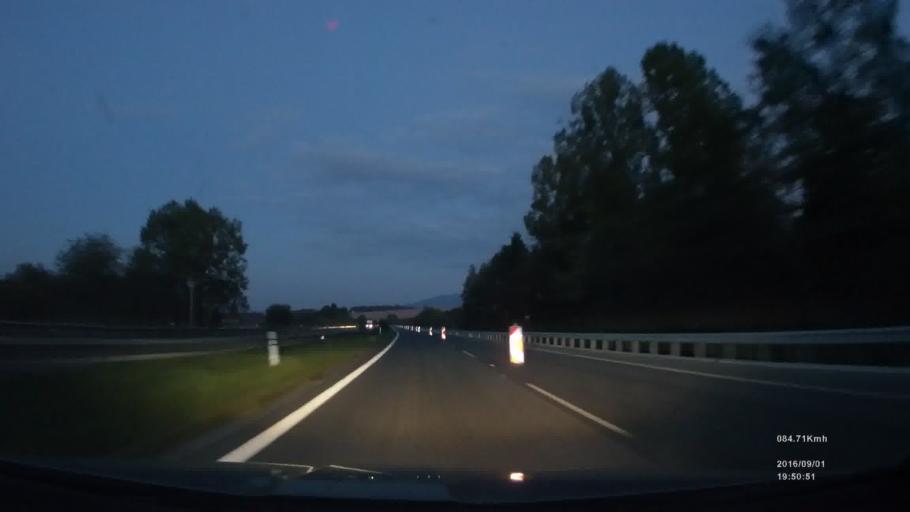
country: SK
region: Zilinsky
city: Ruzomberok
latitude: 49.0912
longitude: 19.4497
